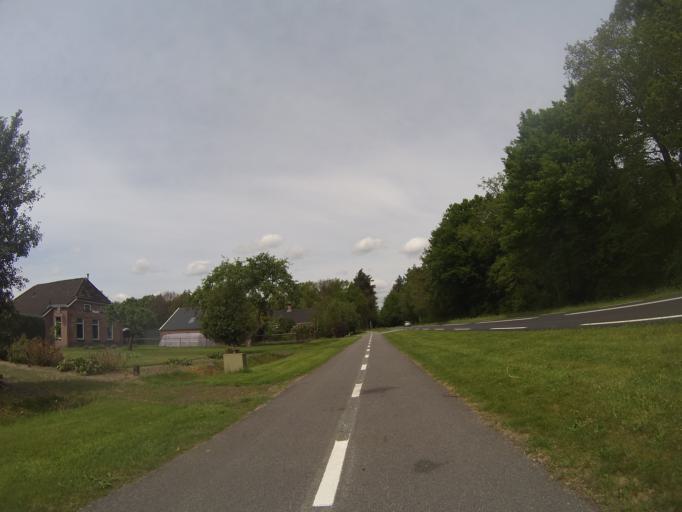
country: NL
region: Drenthe
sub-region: Gemeente Borger-Odoorn
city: Borger
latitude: 52.8804
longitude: 6.7195
